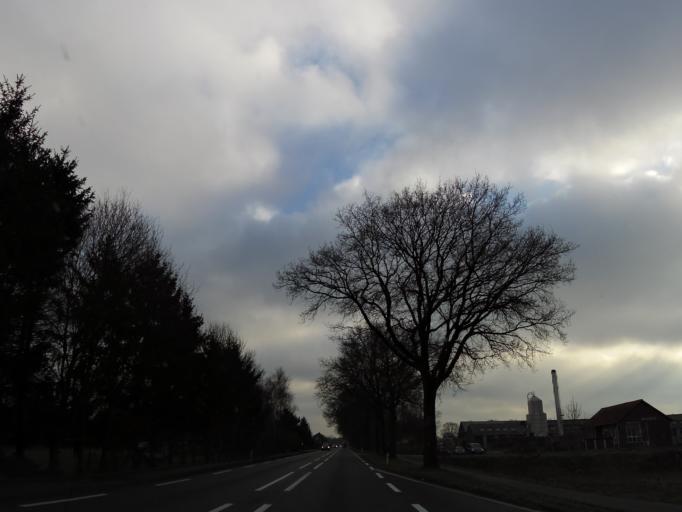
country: NL
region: North Brabant
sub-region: Gemeente Boxmeer
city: Boxmeer
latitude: 51.6248
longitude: 6.0251
